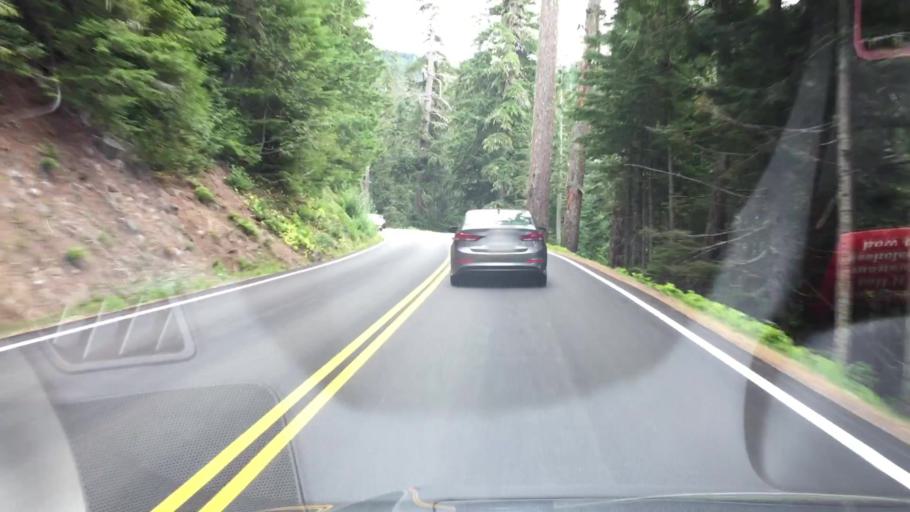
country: US
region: Washington
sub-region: Pierce County
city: Buckley
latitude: 46.7796
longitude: -121.7758
